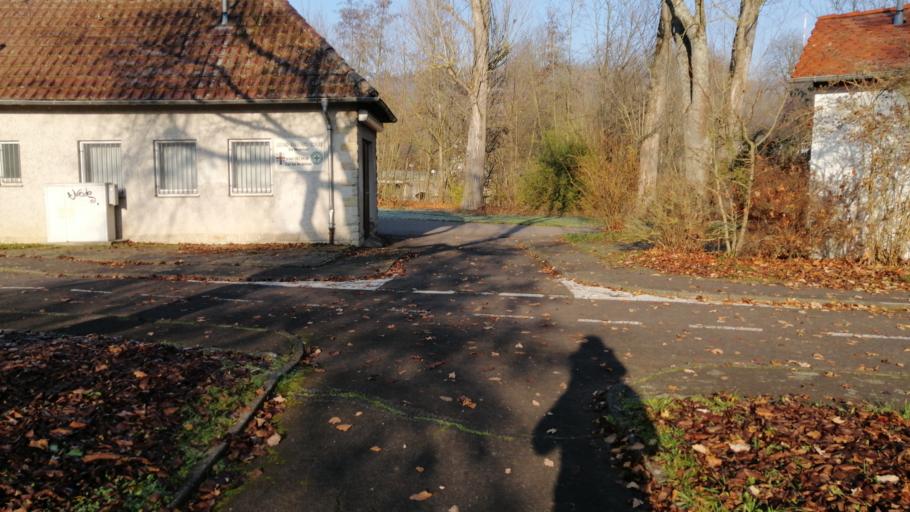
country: DE
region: Baden-Wuerttemberg
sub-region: Regierungsbezirk Stuttgart
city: Bad Mergentheim
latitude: 49.4919
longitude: 9.7831
